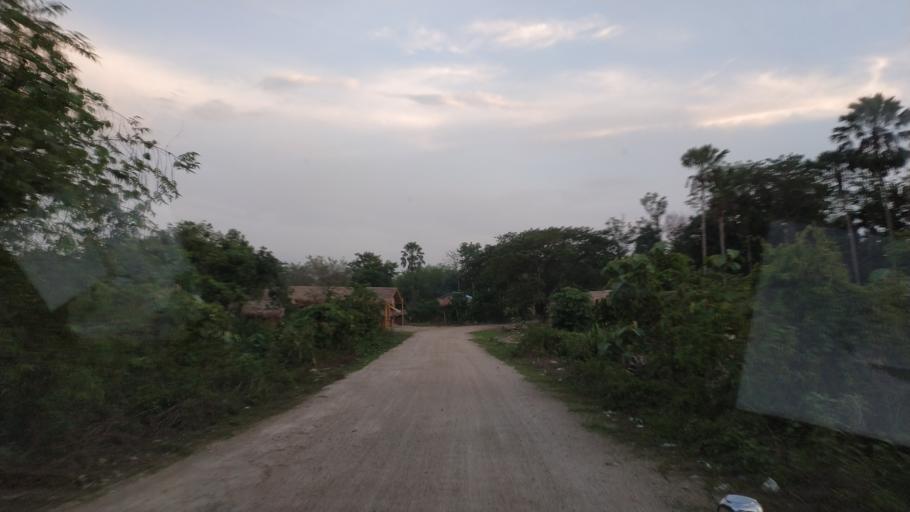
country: MM
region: Mon
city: Kyaikto
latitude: 17.4330
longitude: 97.0404
